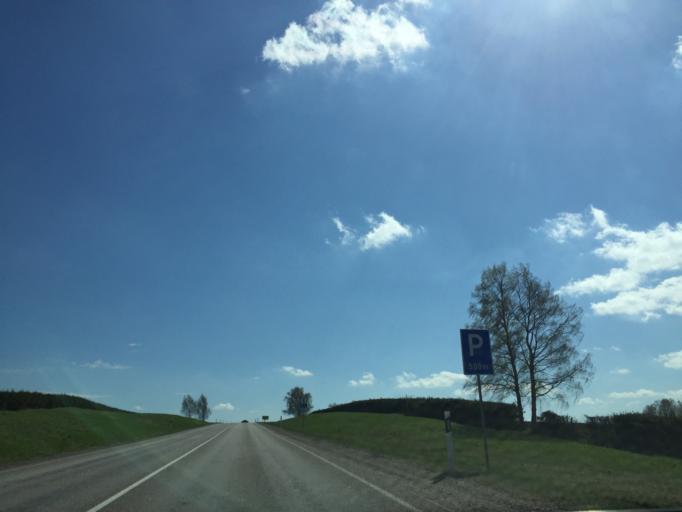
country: EE
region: Tartu
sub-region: Elva linn
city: Elva
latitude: 58.1137
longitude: 26.2397
